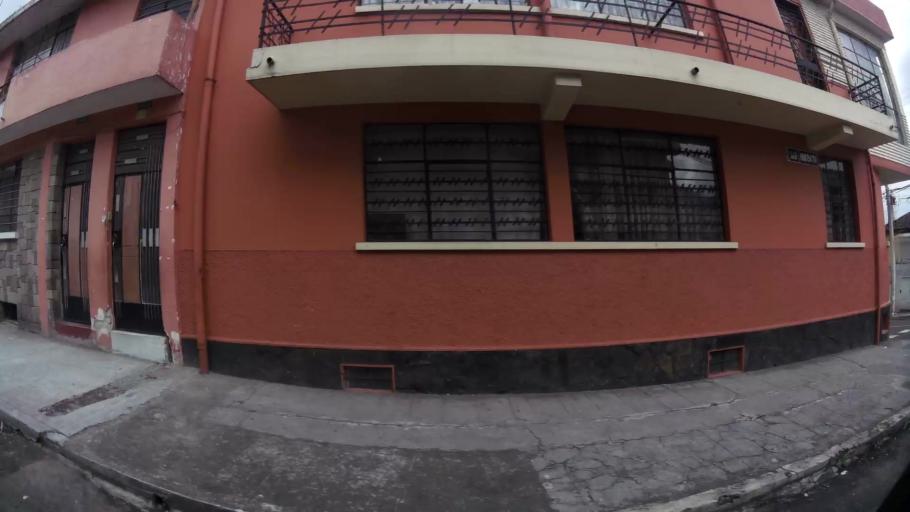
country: EC
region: Pichincha
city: Quito
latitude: -0.2433
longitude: -78.5259
